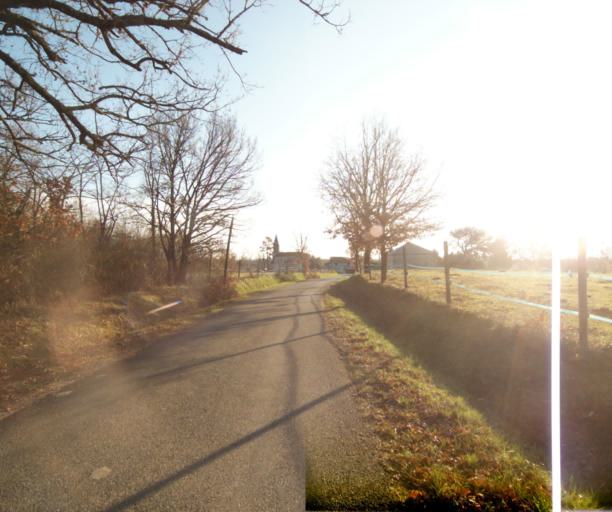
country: FR
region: Midi-Pyrenees
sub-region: Departement du Tarn-et-Garonne
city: Moissac
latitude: 44.1495
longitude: 1.1410
